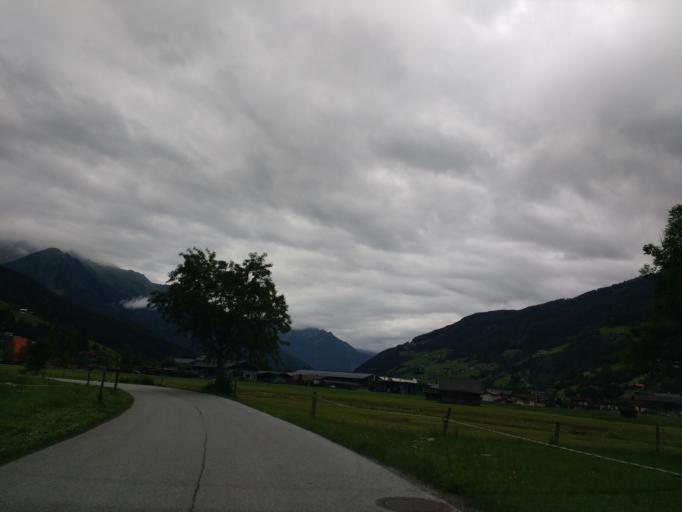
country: AT
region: Salzburg
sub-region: Politischer Bezirk Zell am See
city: Bramberg am Wildkogel
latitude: 47.2766
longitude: 12.3621
